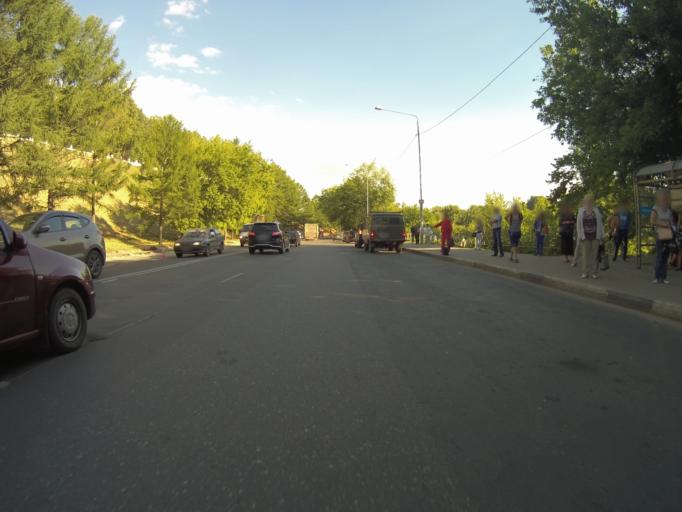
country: RU
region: Vladimir
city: Vladimir
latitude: 56.1272
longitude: 40.4065
